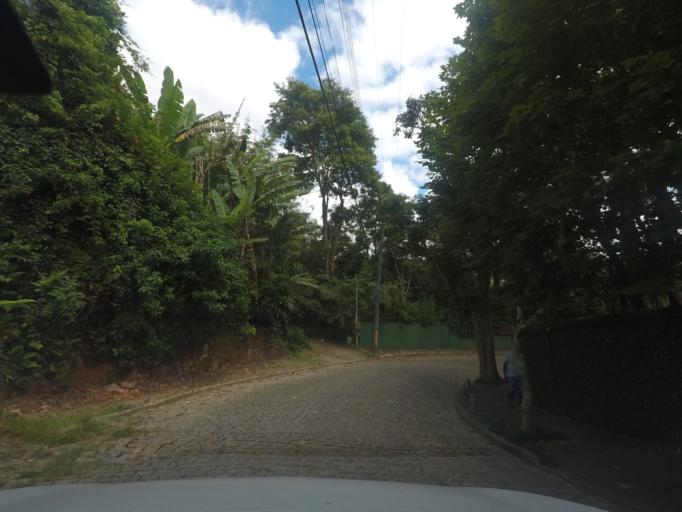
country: BR
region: Rio de Janeiro
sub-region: Teresopolis
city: Teresopolis
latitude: -22.3972
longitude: -42.9860
